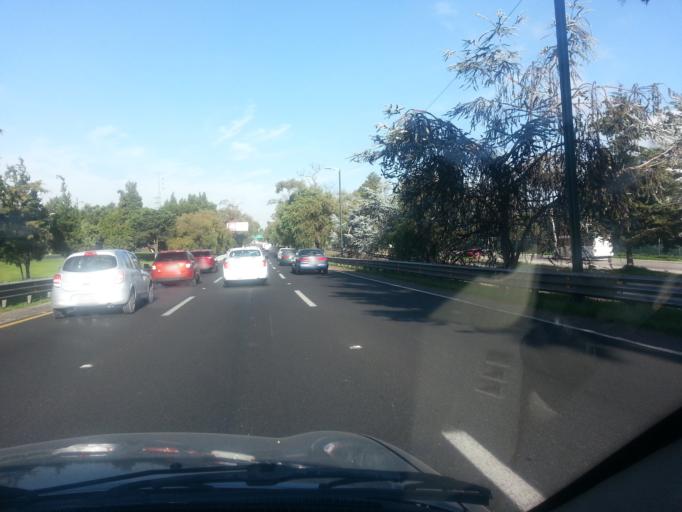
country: MX
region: Mexico
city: Santa Maria Totoltepec
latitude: 19.2876
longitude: -99.5964
